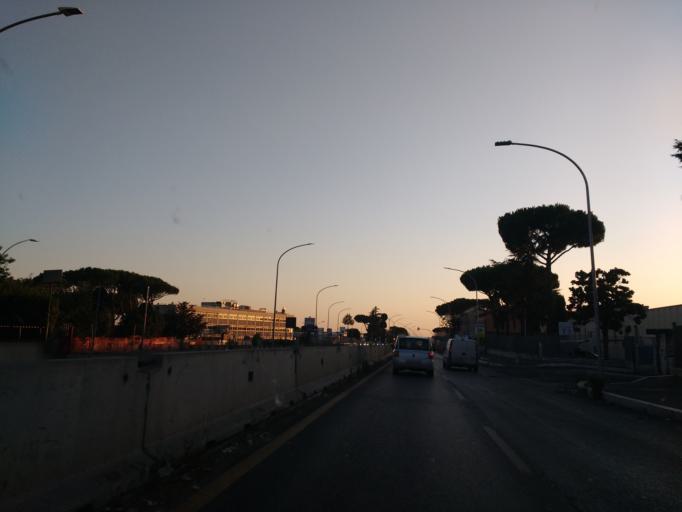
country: IT
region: Latium
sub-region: Citta metropolitana di Roma Capitale
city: Setteville
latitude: 41.9377
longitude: 12.6193
